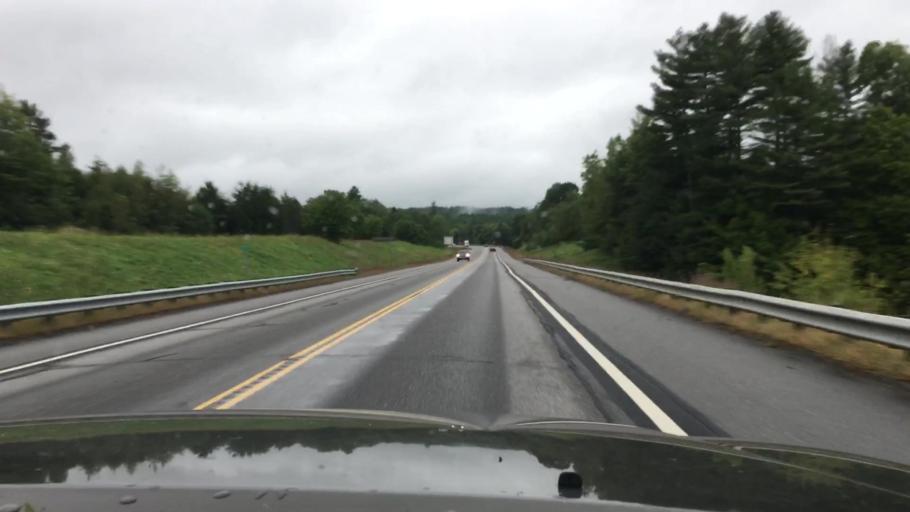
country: US
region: New Hampshire
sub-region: Hillsborough County
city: Hillsborough
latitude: 43.1174
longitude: -71.9307
